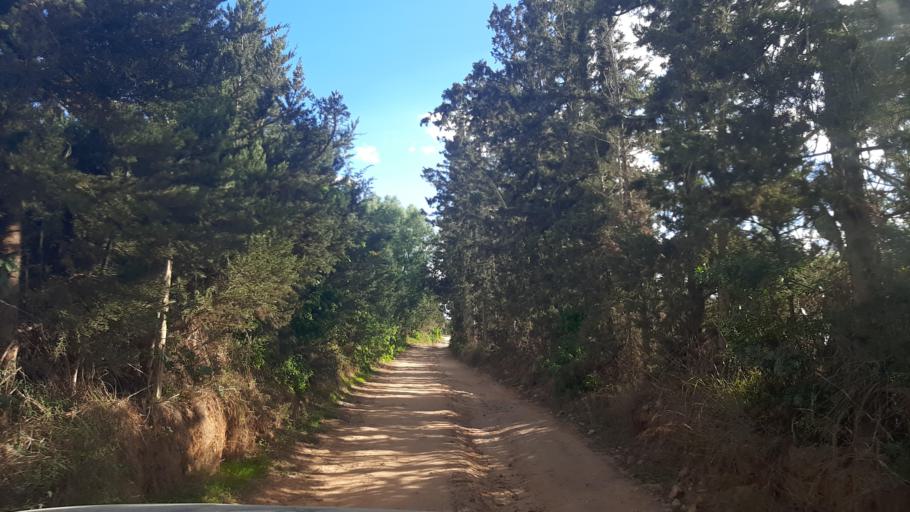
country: TN
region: Nabul
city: Bu `Urqub
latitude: 36.4325
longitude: 10.5048
